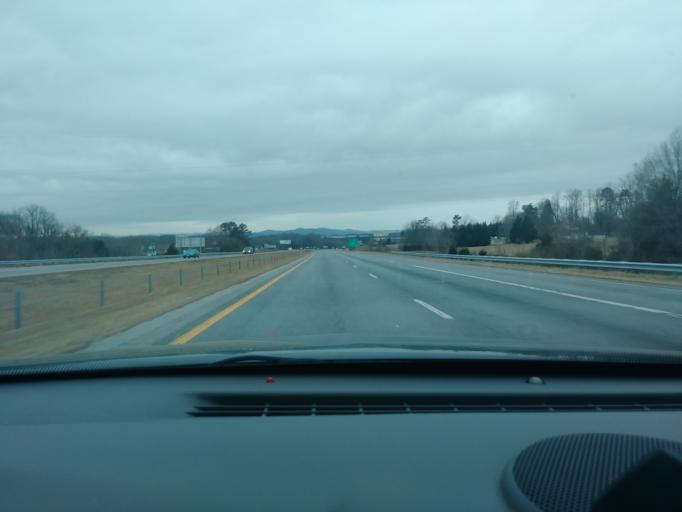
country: US
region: North Carolina
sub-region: Yadkin County
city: Jonesville
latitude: 36.1194
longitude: -80.7979
